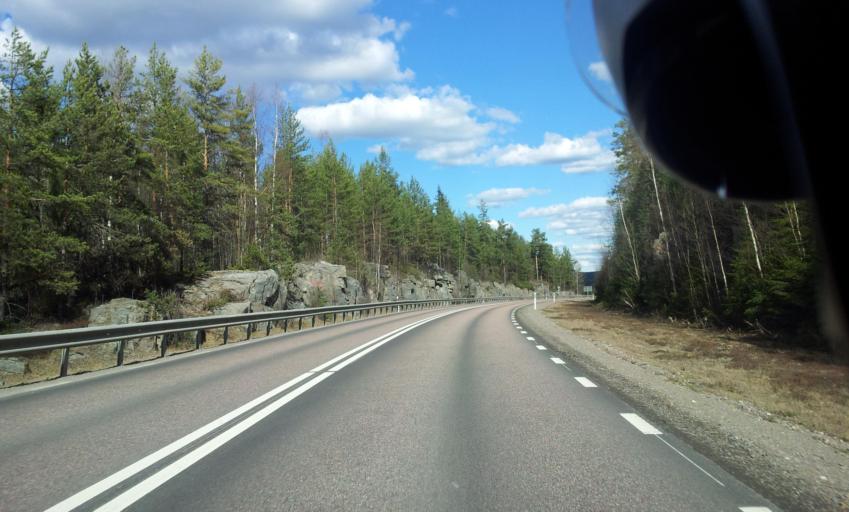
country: SE
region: Gaevleborg
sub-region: Ljusdals Kommun
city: Ljusdal
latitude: 61.8239
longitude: 16.0310
